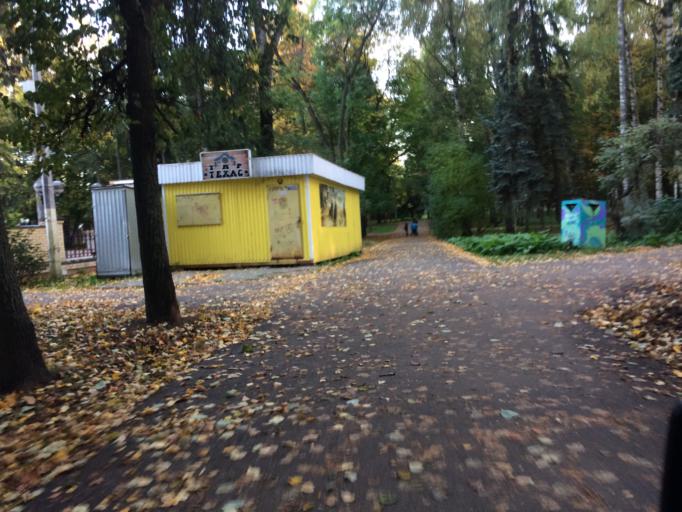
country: RU
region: Mariy-El
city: Yoshkar-Ola
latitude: 56.6356
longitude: 47.8916
